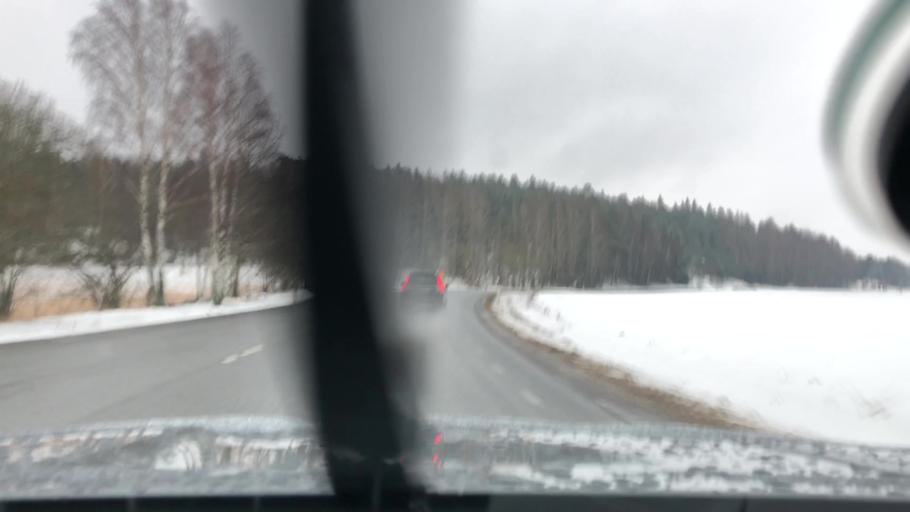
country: SE
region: Stockholm
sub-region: Sodertalje Kommun
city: Pershagen
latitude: 59.0598
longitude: 17.6128
